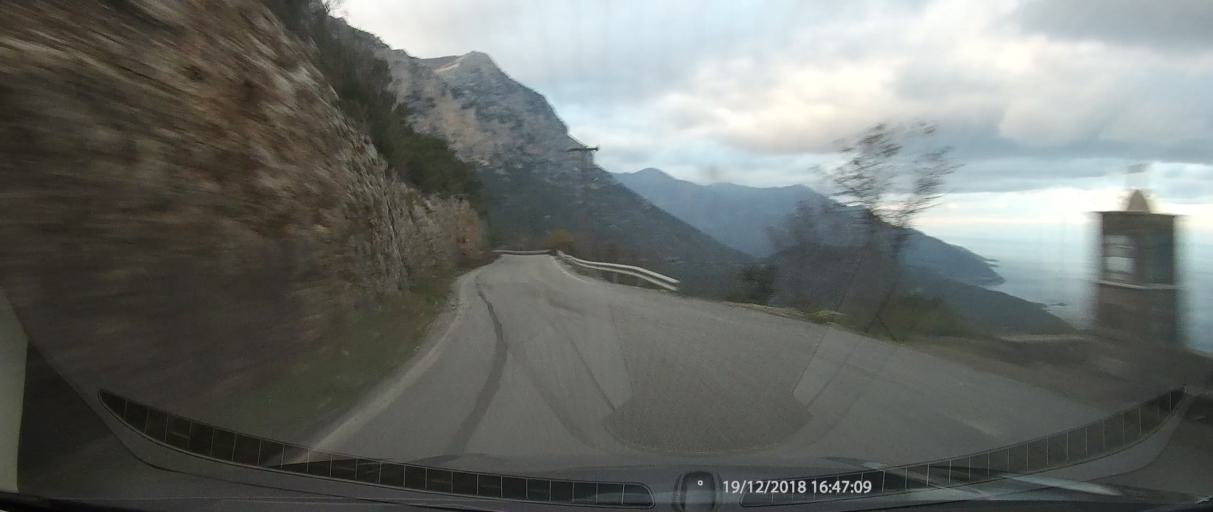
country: GR
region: Peloponnese
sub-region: Nomos Lakonias
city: Sykea
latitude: 36.9269
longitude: 23.0068
